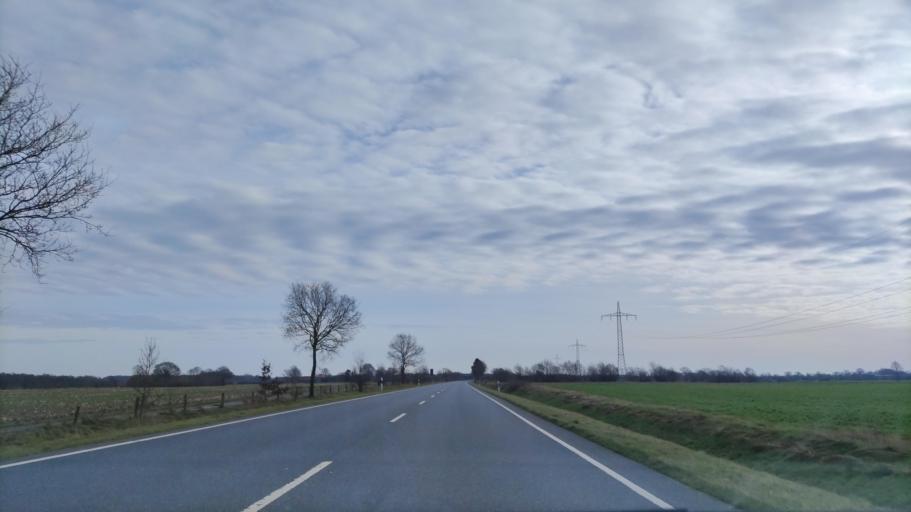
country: DE
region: Schleswig-Holstein
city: Bokel
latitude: 54.1928
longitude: 9.7993
